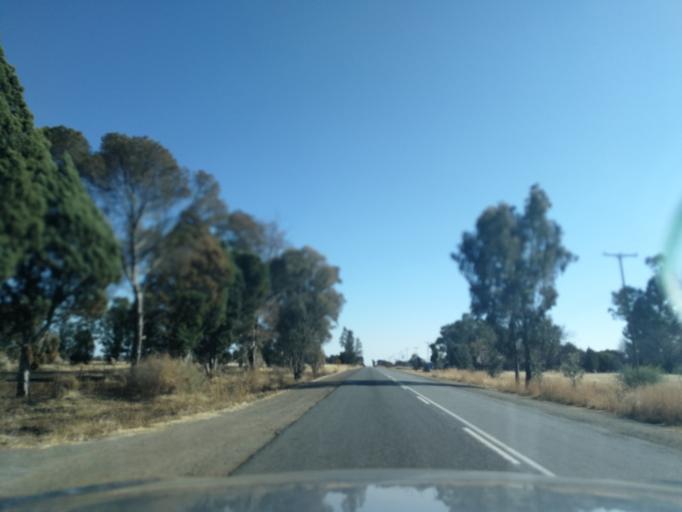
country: ZA
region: Orange Free State
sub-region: Fezile Dabi District Municipality
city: Kroonstad
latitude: -27.6239
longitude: 27.2125
